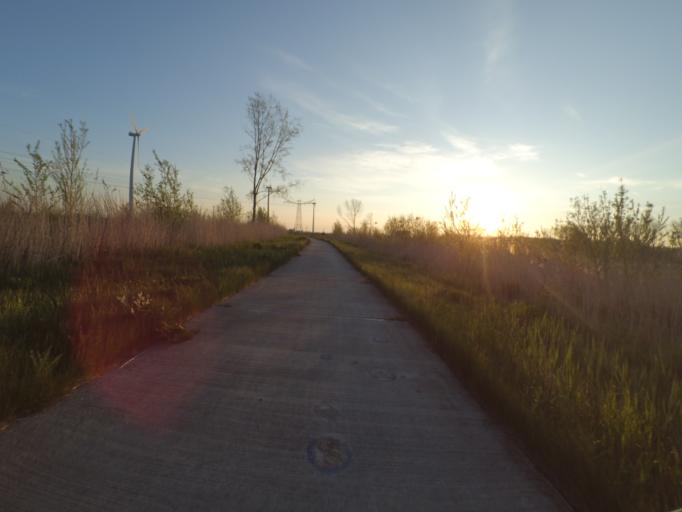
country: NL
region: Flevoland
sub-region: Gemeente Zeewolde
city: Zeewolde
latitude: 52.3341
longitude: 5.4351
